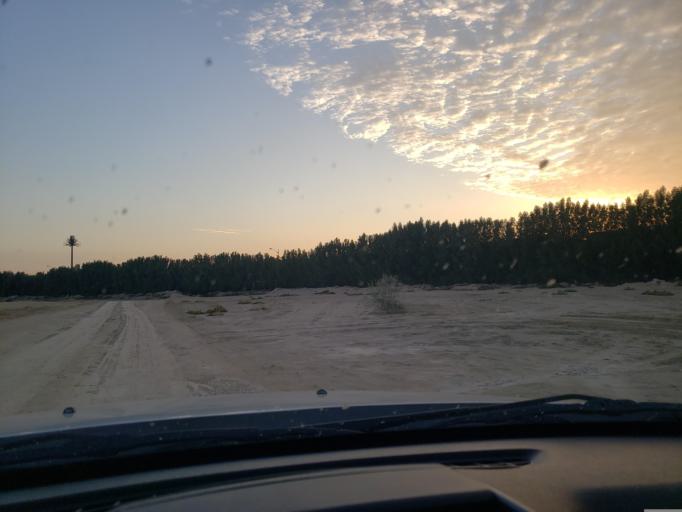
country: AE
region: Dubai
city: Dubai
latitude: 25.0181
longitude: 55.2620
